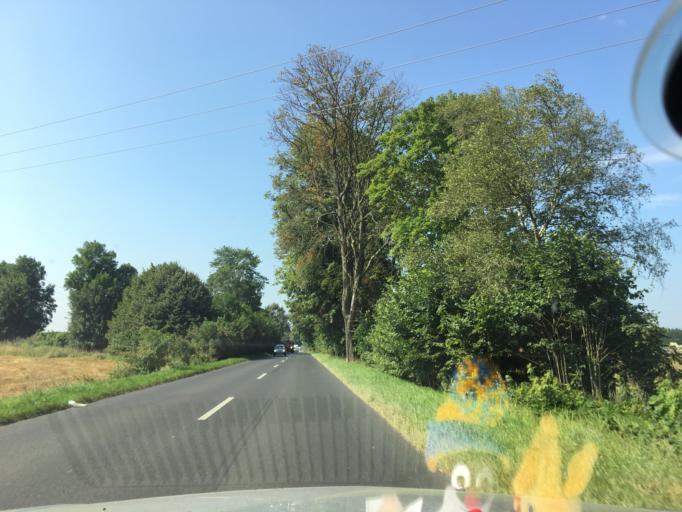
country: PL
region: West Pomeranian Voivodeship
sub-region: Powiat kamienski
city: Kamien Pomorski
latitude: 53.9954
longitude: 14.8219
